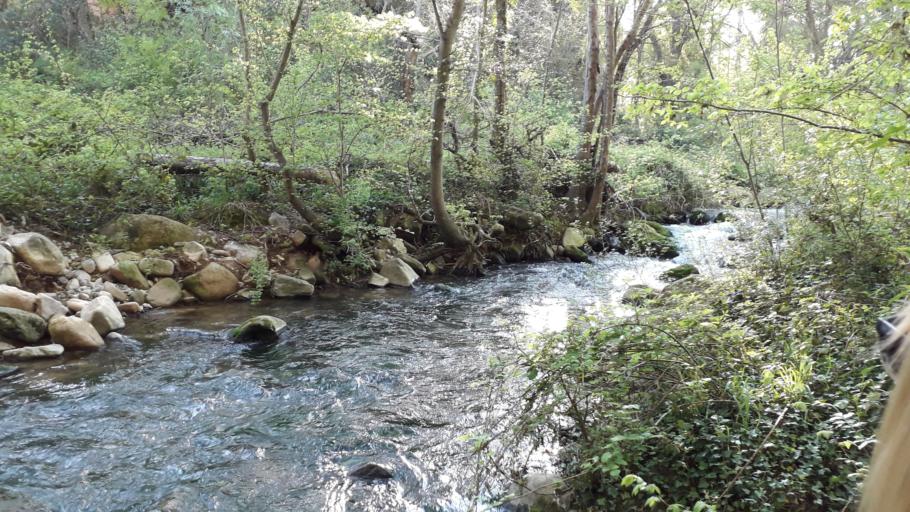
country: ES
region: Catalonia
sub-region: Provincia de Barcelona
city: Jorba
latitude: 41.5922
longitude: 1.5524
